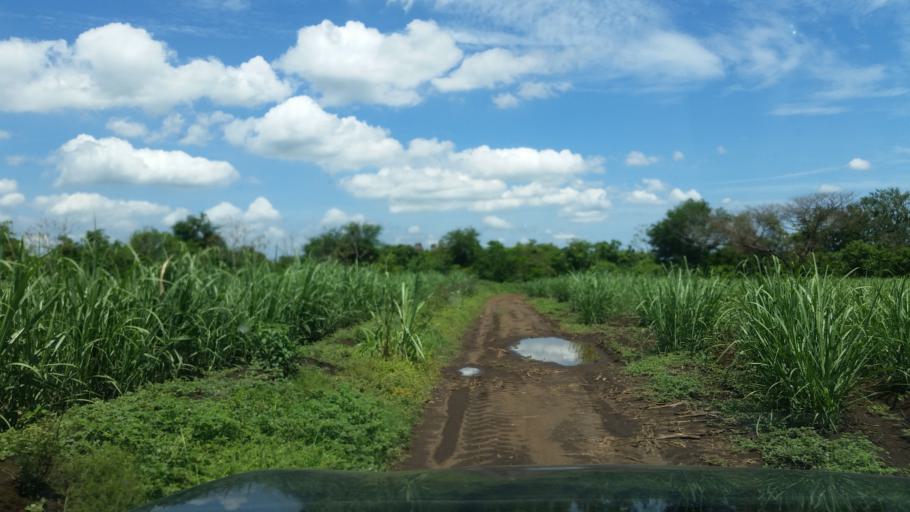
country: NI
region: Chinandega
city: Puerto Morazan
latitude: 12.7720
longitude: -87.1242
